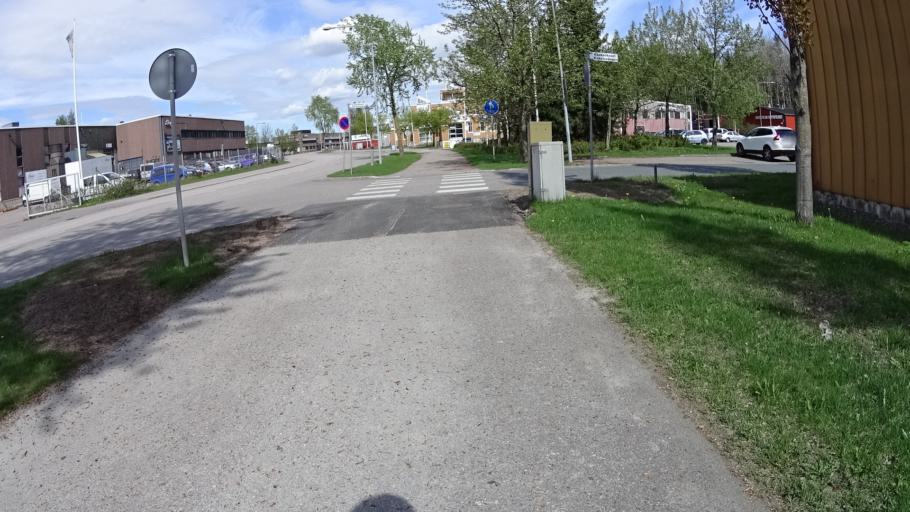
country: FI
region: Uusimaa
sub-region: Helsinki
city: Kilo
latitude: 60.2805
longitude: 24.8172
